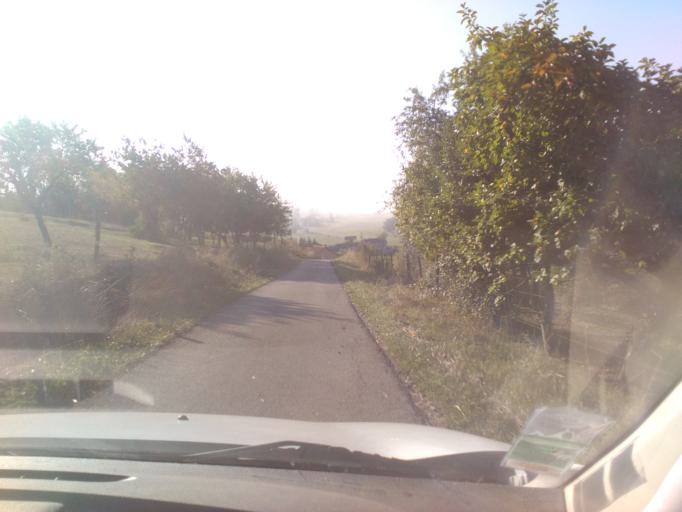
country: FR
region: Lorraine
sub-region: Departement des Vosges
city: Mirecourt
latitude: 48.2603
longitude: 6.1856
